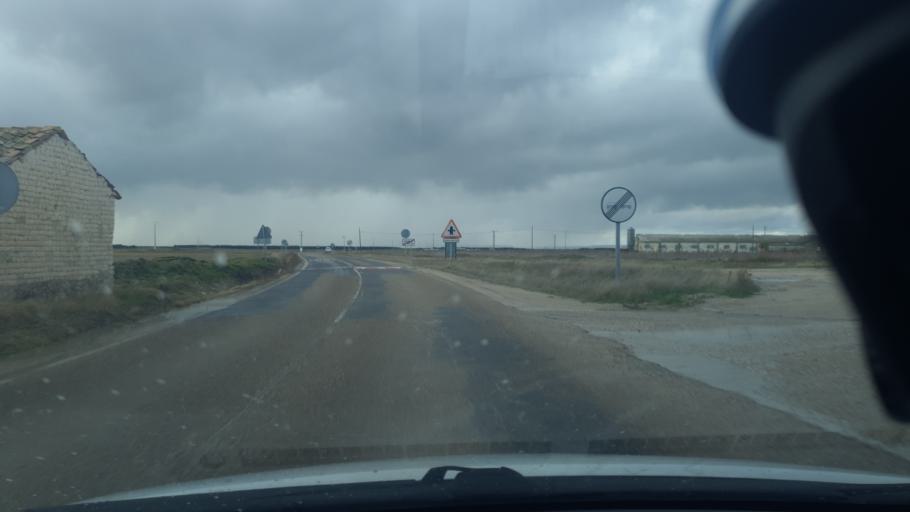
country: ES
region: Castille and Leon
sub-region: Provincia de Segovia
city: Sanchonuno
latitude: 41.3110
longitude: -4.3671
